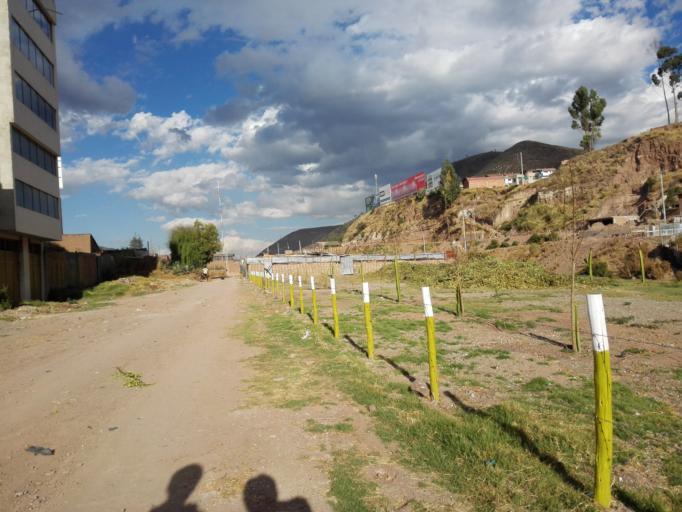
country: PE
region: Cusco
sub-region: Provincia de Cusco
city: Cusco
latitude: -13.5390
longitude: -71.9470
